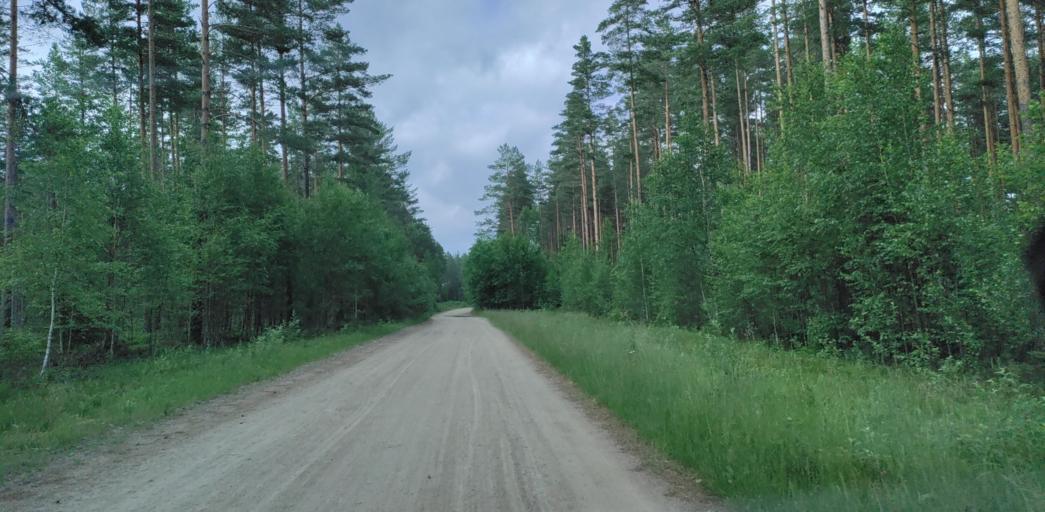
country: SE
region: Vaermland
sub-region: Hagfors Kommun
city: Hagfors
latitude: 60.0505
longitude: 13.5797
